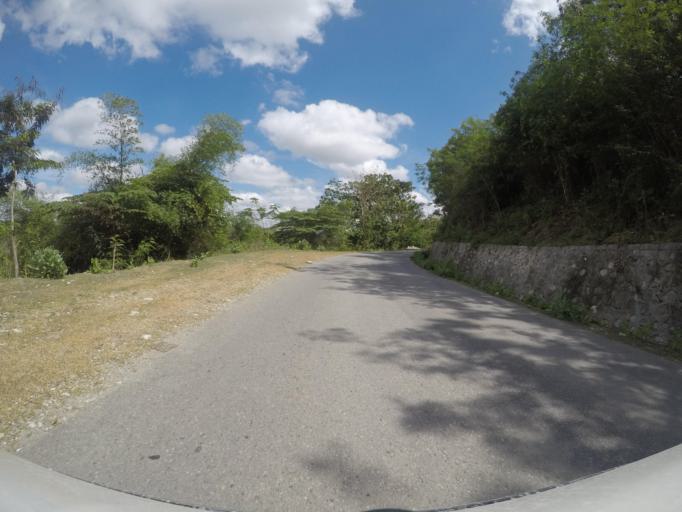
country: TL
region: Viqueque
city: Viqueque
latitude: -8.8737
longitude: 126.3568
